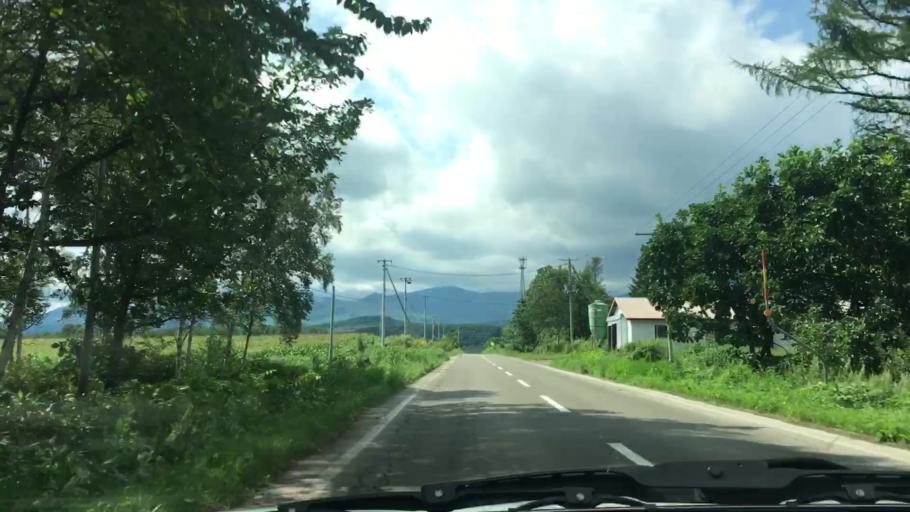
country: JP
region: Hokkaido
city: Otofuke
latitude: 43.2831
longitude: 143.3163
